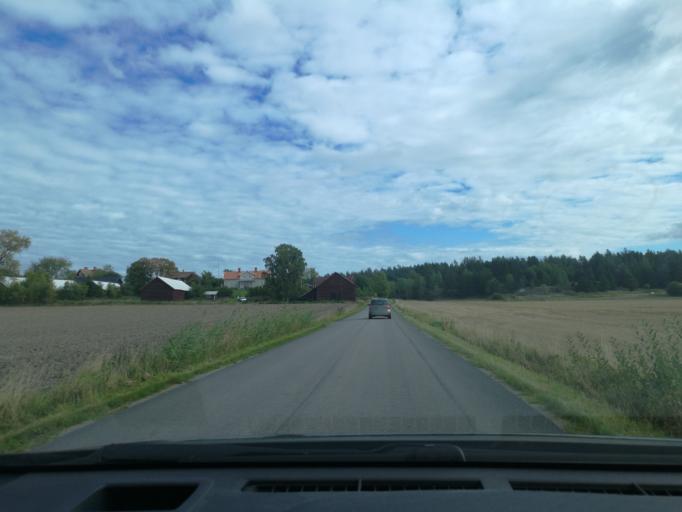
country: SE
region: OEstergoetland
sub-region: Soderkopings Kommun
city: Soederkoeping
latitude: 58.5190
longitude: 16.4100
